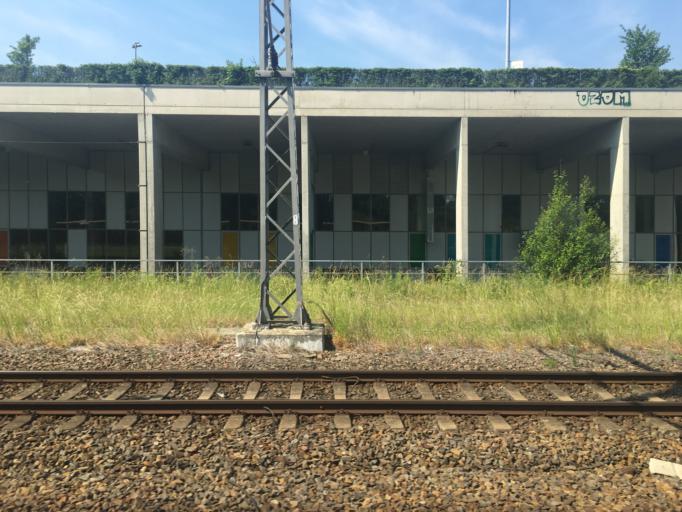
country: DE
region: Berlin
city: Friedrichshain Bezirk
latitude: 52.5310
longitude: 13.4531
